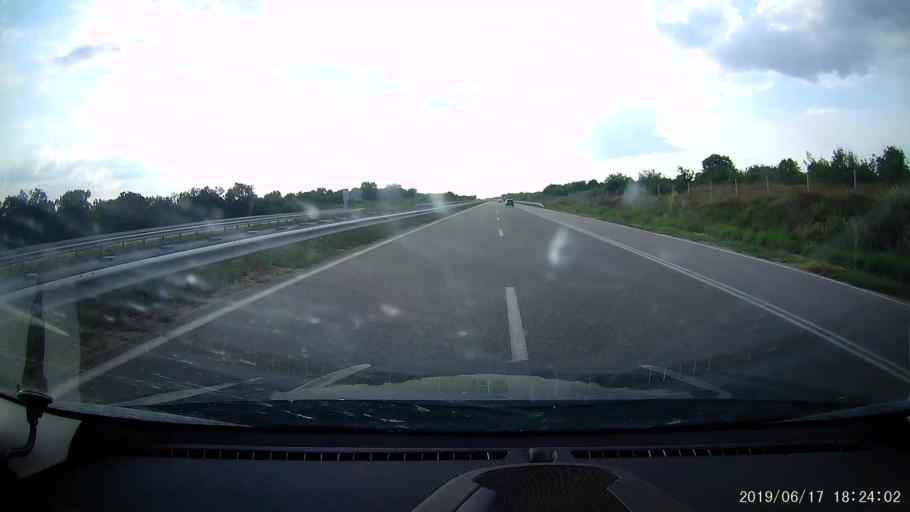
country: BG
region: Khaskovo
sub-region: Obshtina Dimitrovgrad
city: Dimitrovgrad
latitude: 41.9800
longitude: 25.7030
